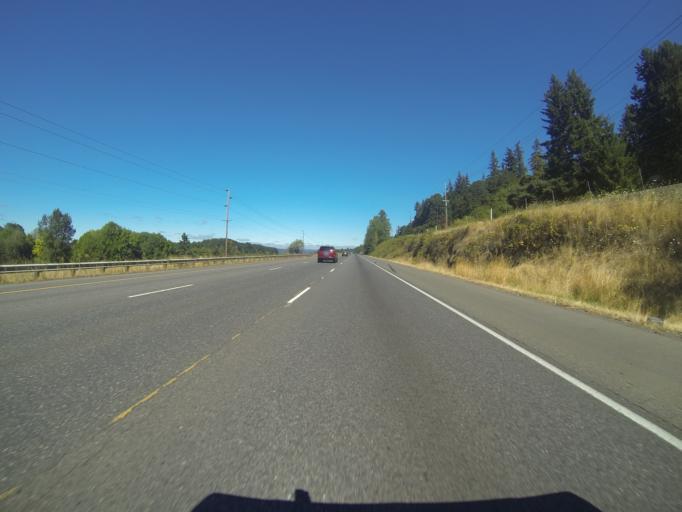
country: US
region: Washington
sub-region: Cowlitz County
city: Woodland
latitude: 45.9485
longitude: -122.7841
